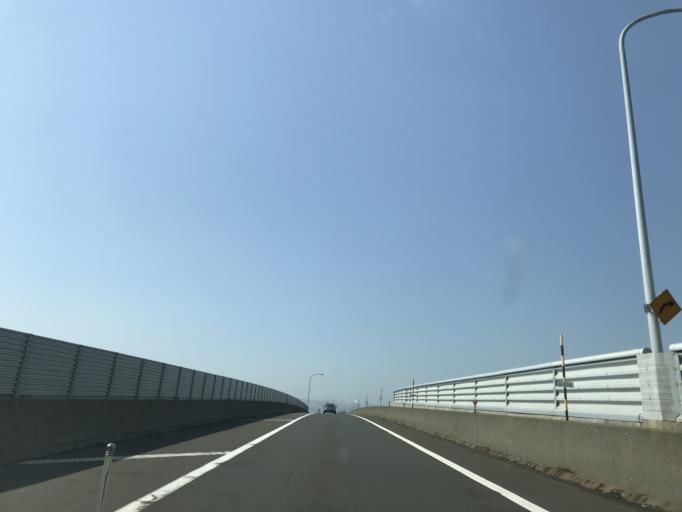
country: JP
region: Hokkaido
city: Sapporo
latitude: 43.0768
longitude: 141.4226
